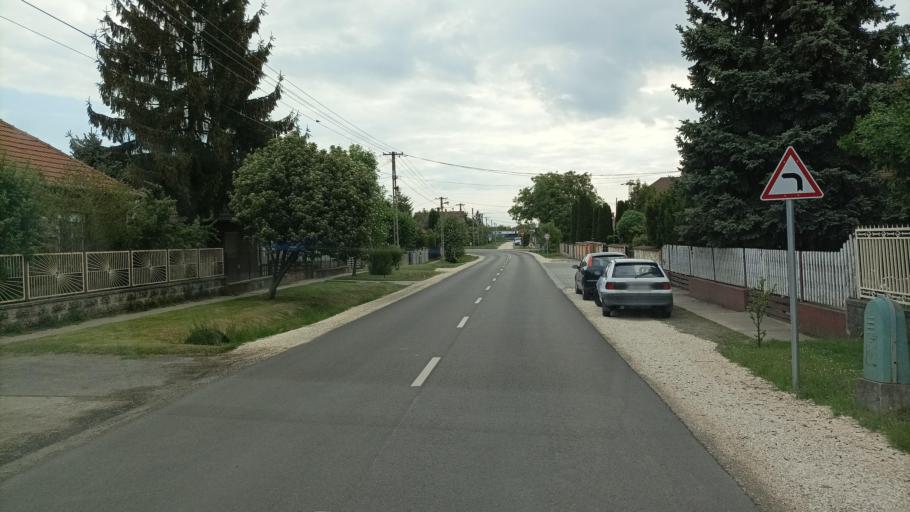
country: HU
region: Pest
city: Pilis
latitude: 47.2789
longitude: 19.5318
